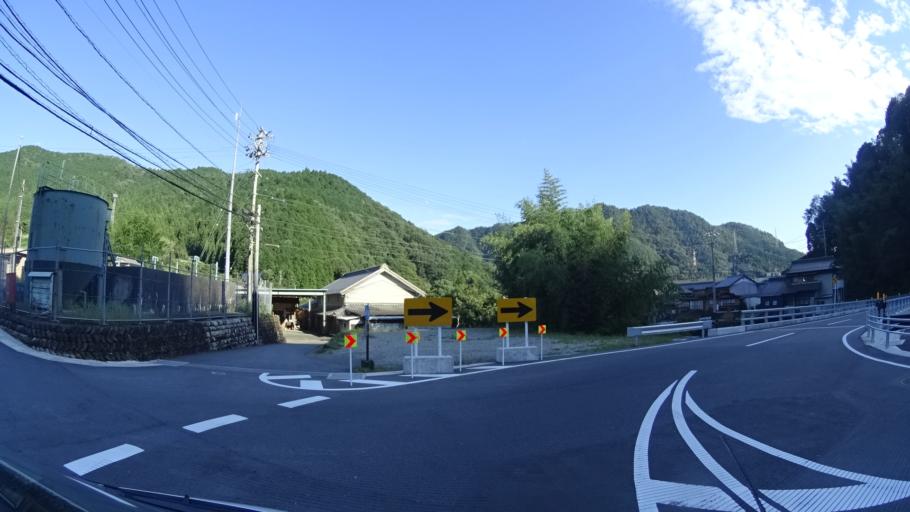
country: JP
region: Gifu
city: Minokamo
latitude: 35.5455
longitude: 137.1204
